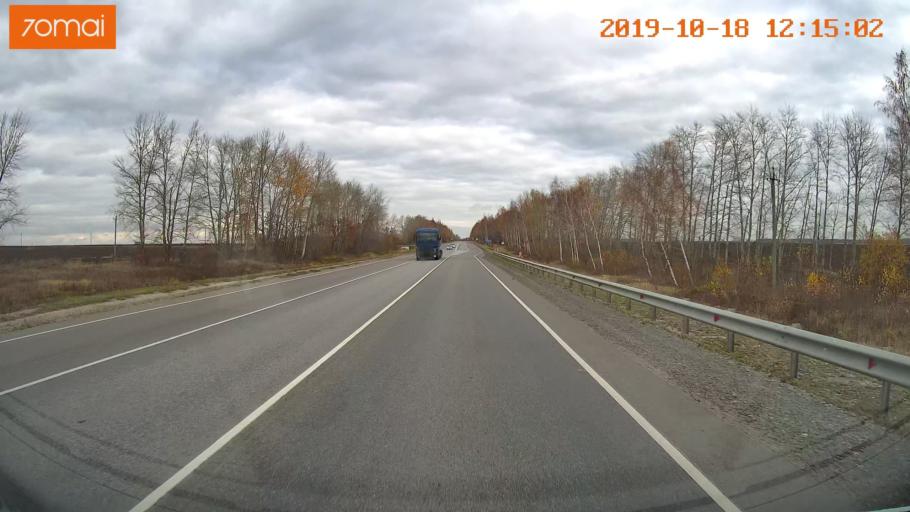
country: RU
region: Rjazan
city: Zakharovo
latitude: 54.4383
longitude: 39.3932
